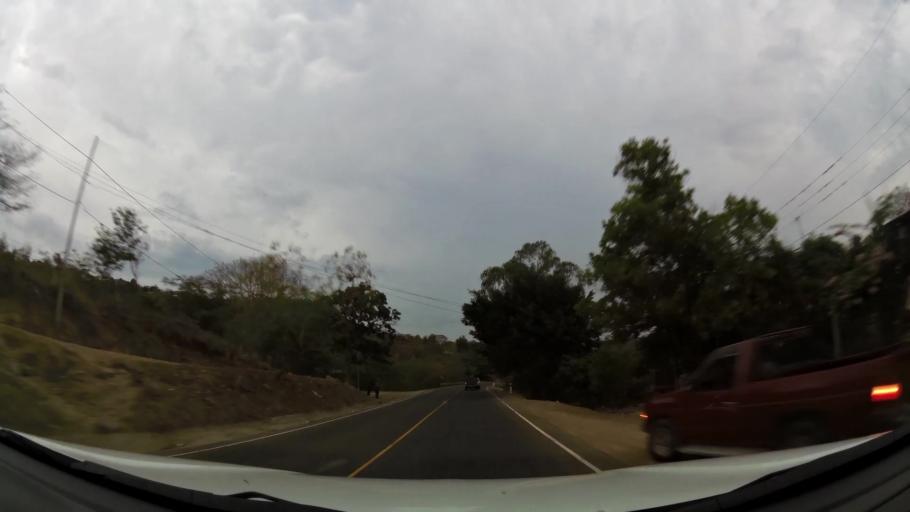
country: NI
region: Esteli
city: Esteli
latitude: 12.9960
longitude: -86.2975
